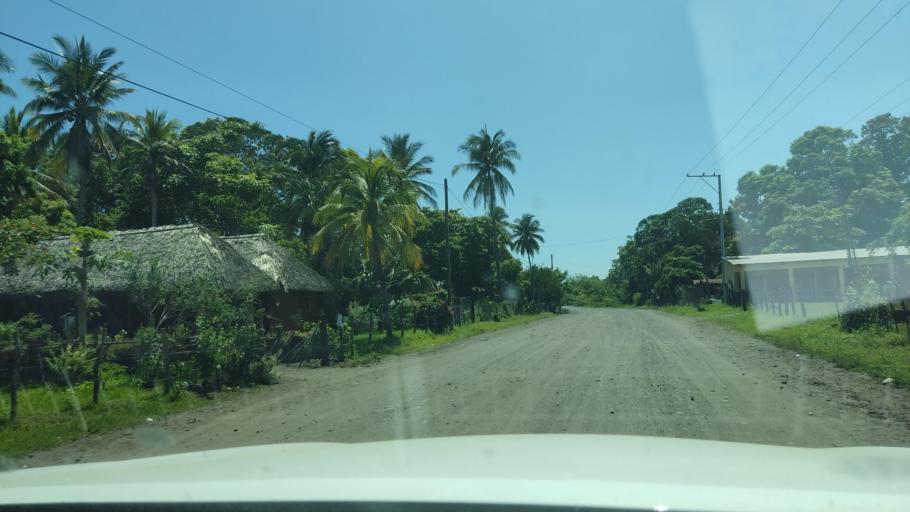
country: SV
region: Ahuachapan
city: San Francisco Menendez
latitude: 13.7651
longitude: -90.1595
